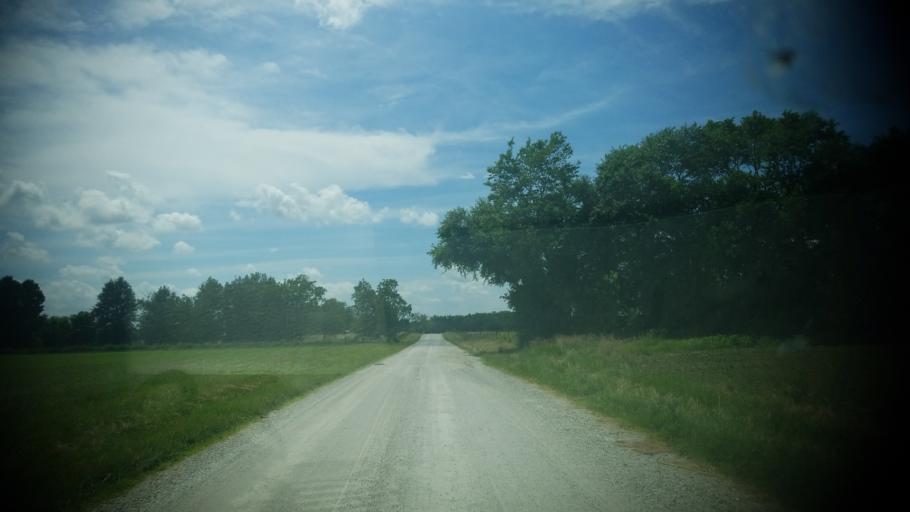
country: US
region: Missouri
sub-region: Pike County
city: Bowling Green
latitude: 39.3091
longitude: -91.3398
